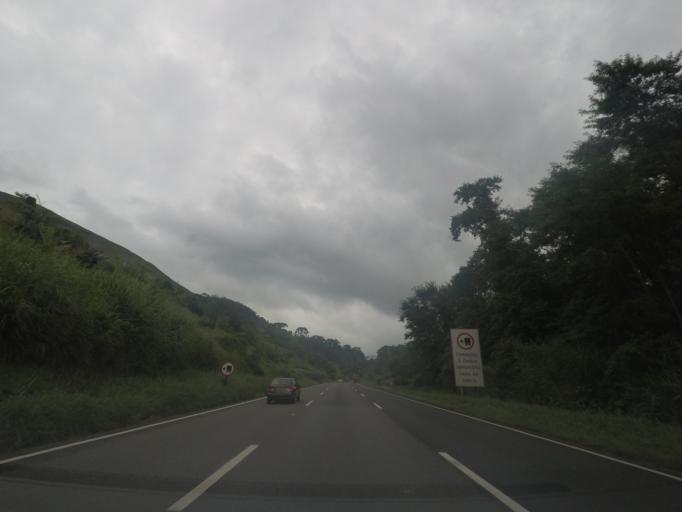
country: BR
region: Sao Paulo
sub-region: Cajati
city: Cajati
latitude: -24.9634
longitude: -48.4791
